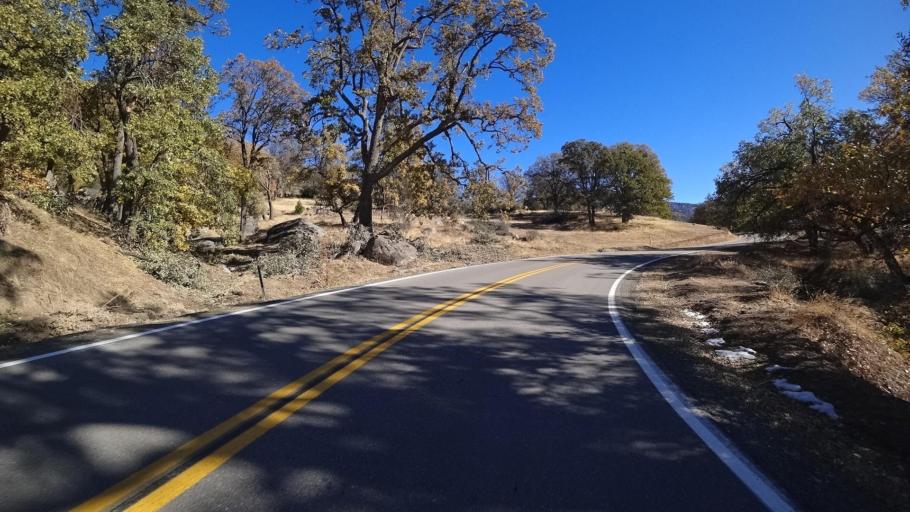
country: US
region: California
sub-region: Kern County
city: Alta Sierra
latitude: 35.7453
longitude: -118.5972
